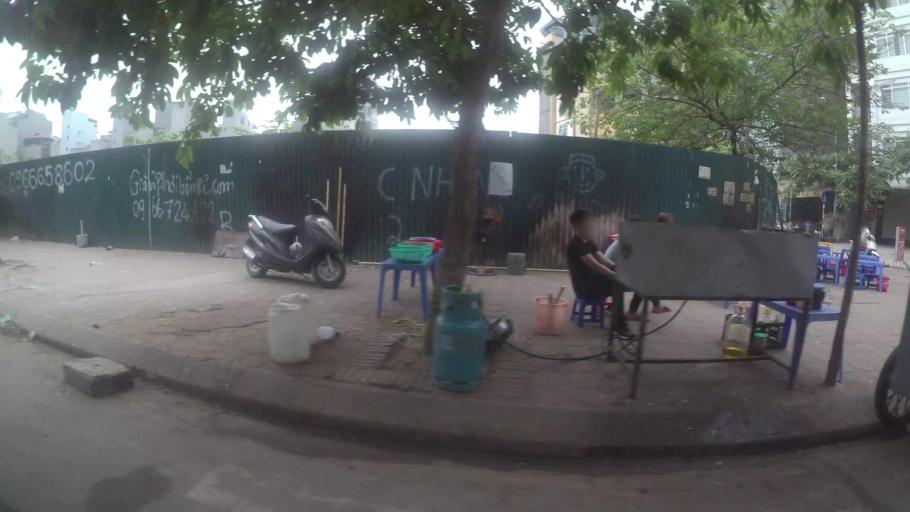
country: VN
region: Ha Noi
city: Cau Dien
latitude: 21.0344
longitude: 105.7729
